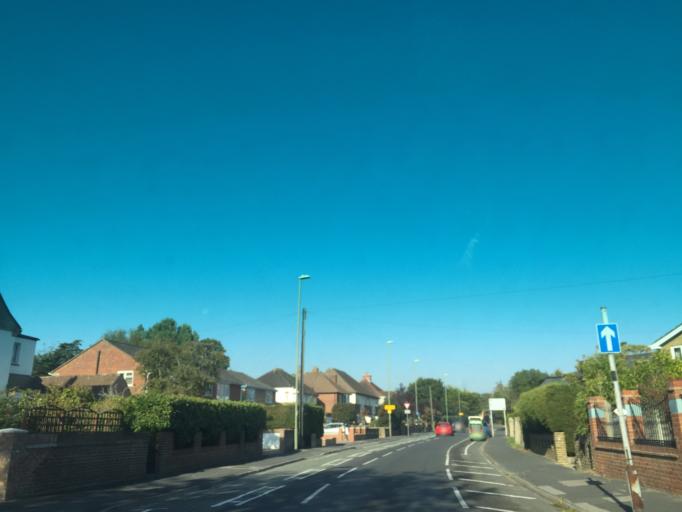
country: GB
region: England
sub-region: Hampshire
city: Gosport
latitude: 50.7912
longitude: -1.1433
